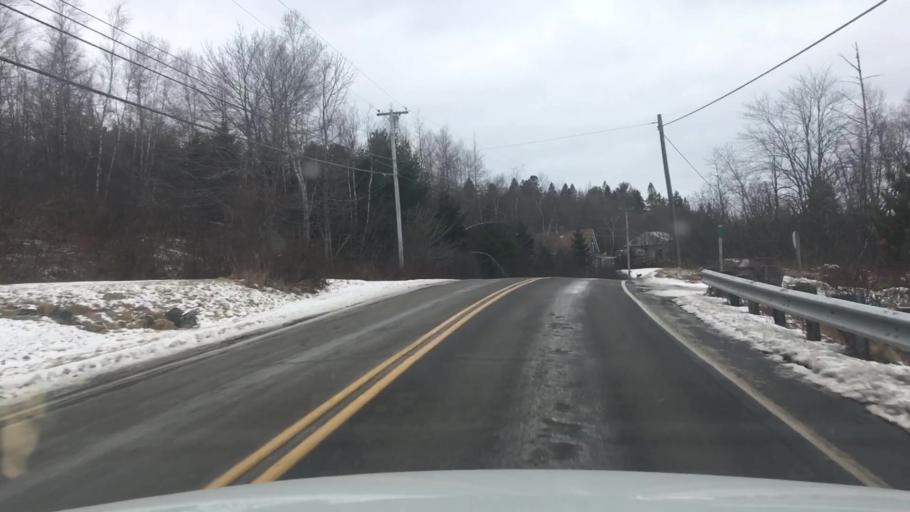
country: US
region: Maine
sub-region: Washington County
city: East Machias
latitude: 44.7267
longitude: -67.3881
